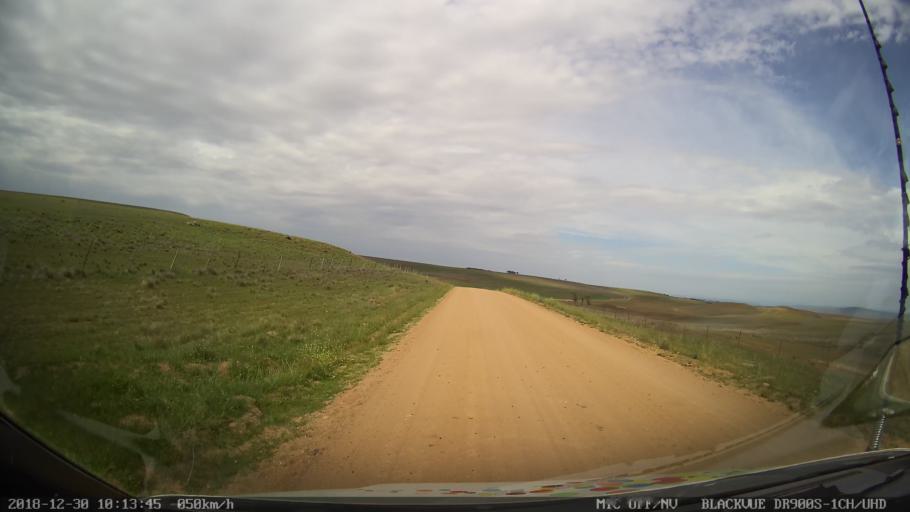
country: AU
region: New South Wales
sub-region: Snowy River
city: Berridale
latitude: -36.5392
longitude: 149.0622
